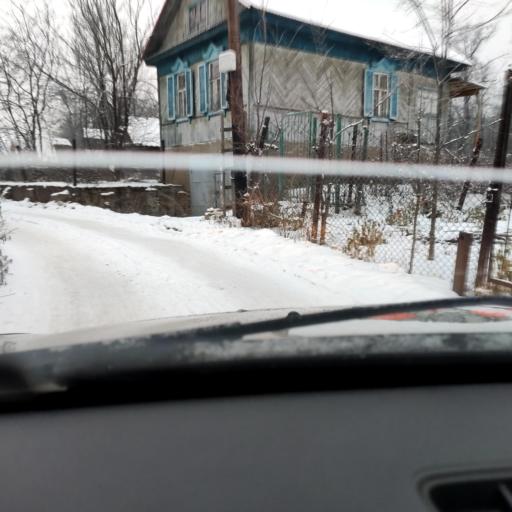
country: RU
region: Bashkortostan
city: Ufa
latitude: 54.6966
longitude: 55.8930
